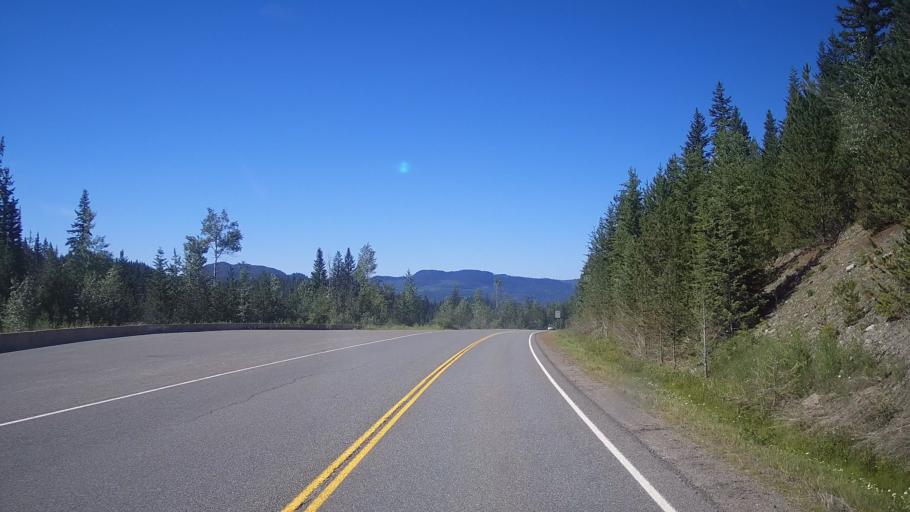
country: CA
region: British Columbia
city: Kamloops
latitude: 51.4946
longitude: -120.4527
